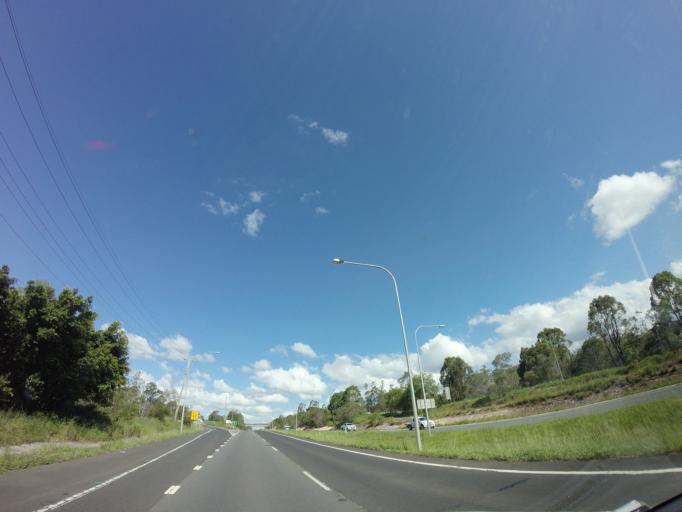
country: AU
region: Queensland
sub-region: Ipswich
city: Riverview
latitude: -27.5903
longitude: 152.8300
